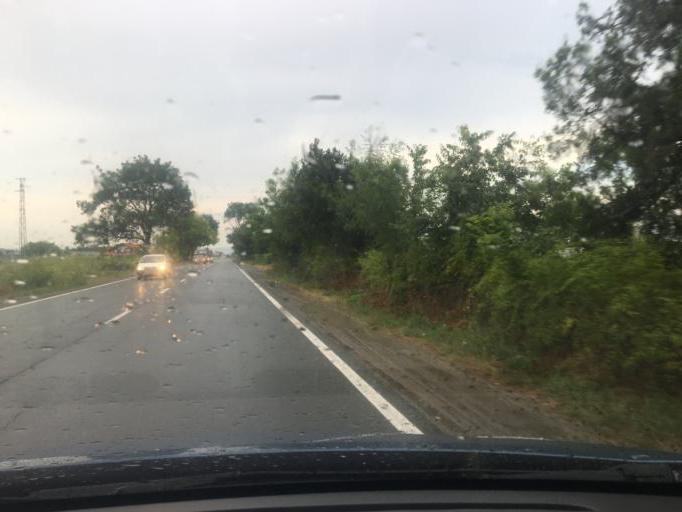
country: BG
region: Burgas
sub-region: Obshtina Pomorie
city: Pomorie
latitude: 42.5713
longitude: 27.6058
